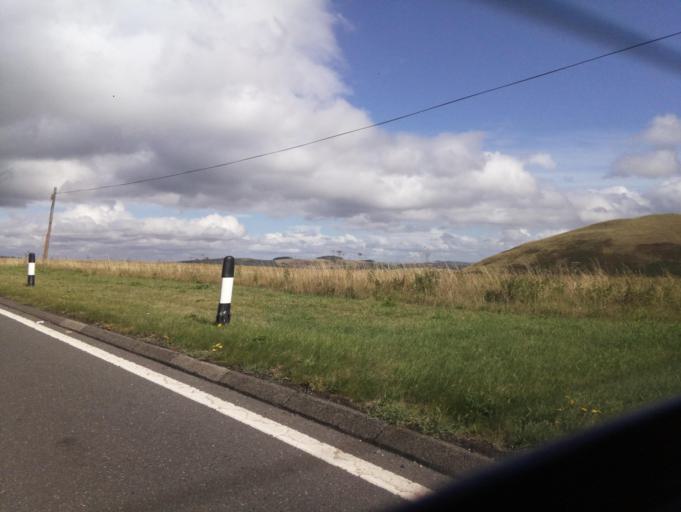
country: GB
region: Scotland
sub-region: The Scottish Borders
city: Jedburgh
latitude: 55.3734
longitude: -2.4911
